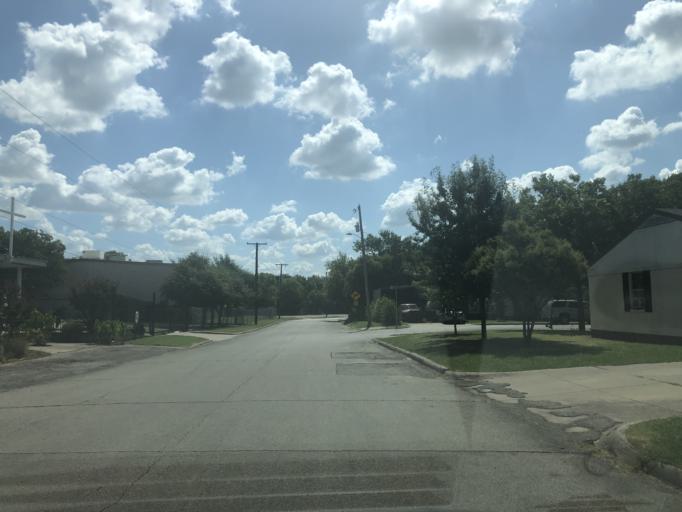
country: US
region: Texas
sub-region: Dallas County
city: Grand Prairie
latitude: 32.7410
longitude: -97.0029
